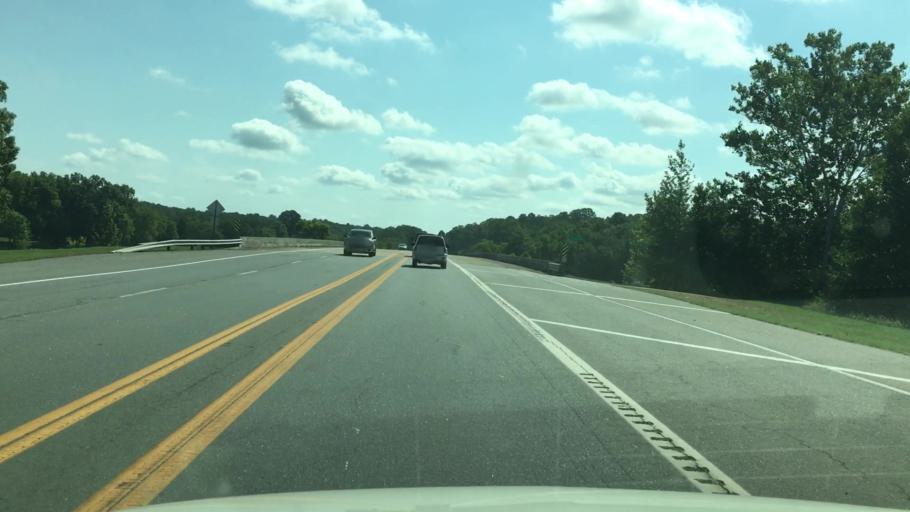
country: US
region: Arkansas
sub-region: Garland County
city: Piney
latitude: 34.5072
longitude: -93.1836
